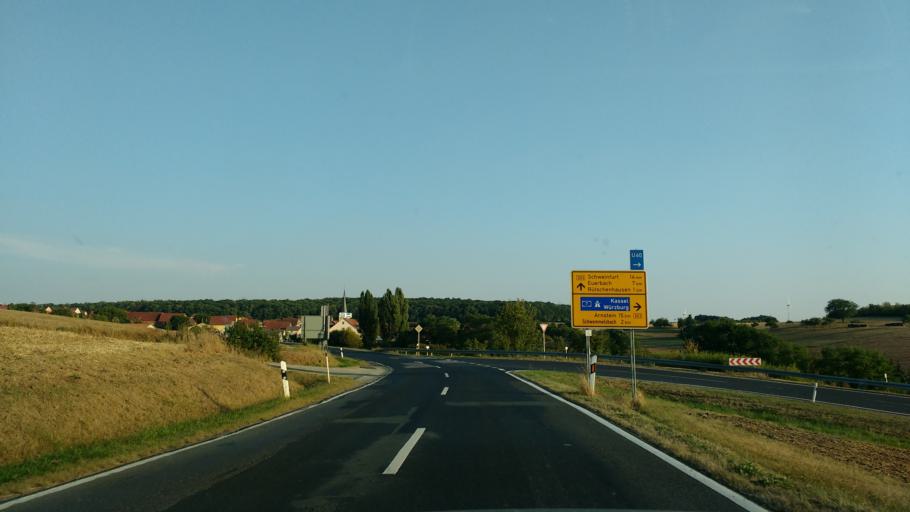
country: DE
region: Bavaria
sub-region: Regierungsbezirk Unterfranken
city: Wasserlosen
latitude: 50.0640
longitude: 10.0520
